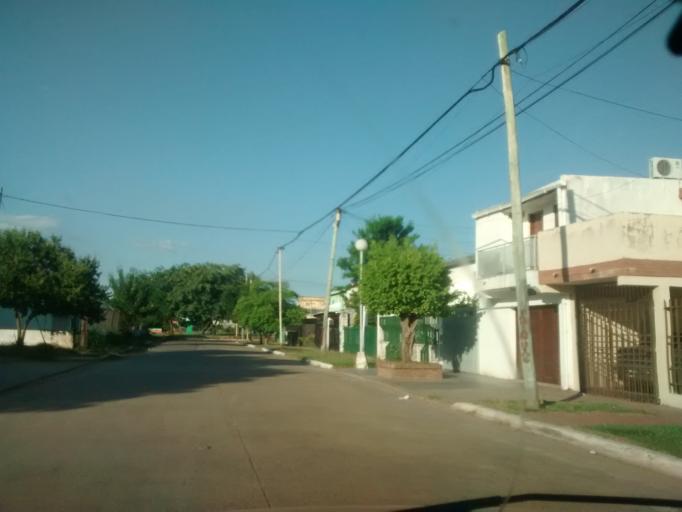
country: AR
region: Chaco
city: Fontana
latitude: -27.4486
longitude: -59.0154
